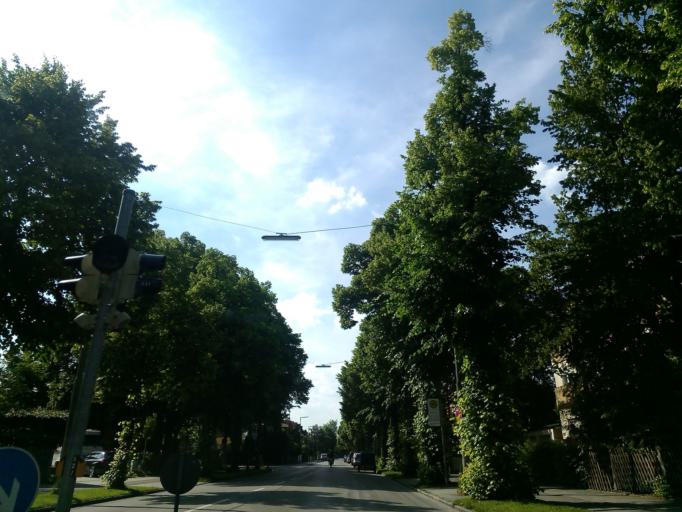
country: DE
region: Bavaria
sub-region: Upper Bavaria
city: Pasing
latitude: 48.1573
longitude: 11.4506
